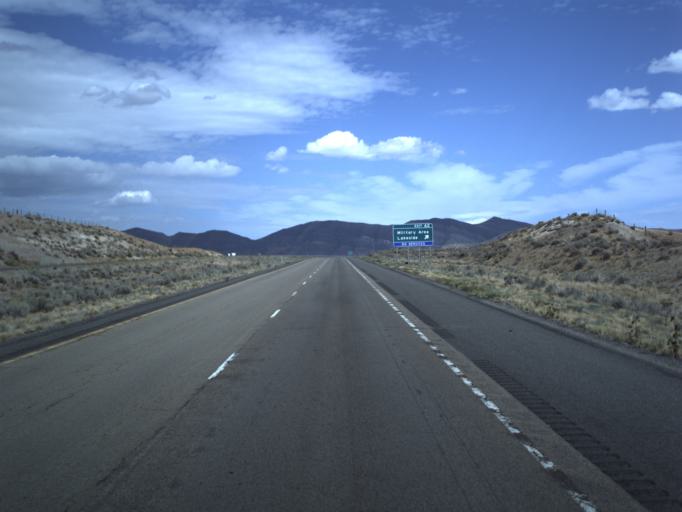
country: US
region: Utah
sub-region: Tooele County
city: Grantsville
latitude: 40.8183
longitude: -112.9113
